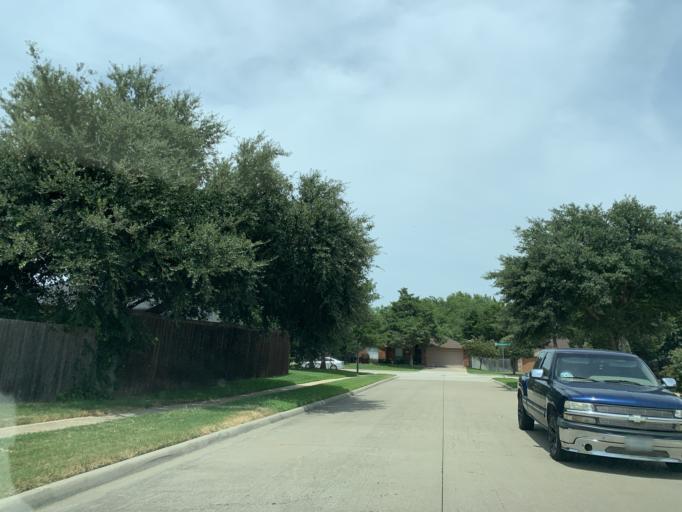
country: US
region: Texas
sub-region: Dallas County
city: Grand Prairie
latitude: 32.6621
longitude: -97.0244
